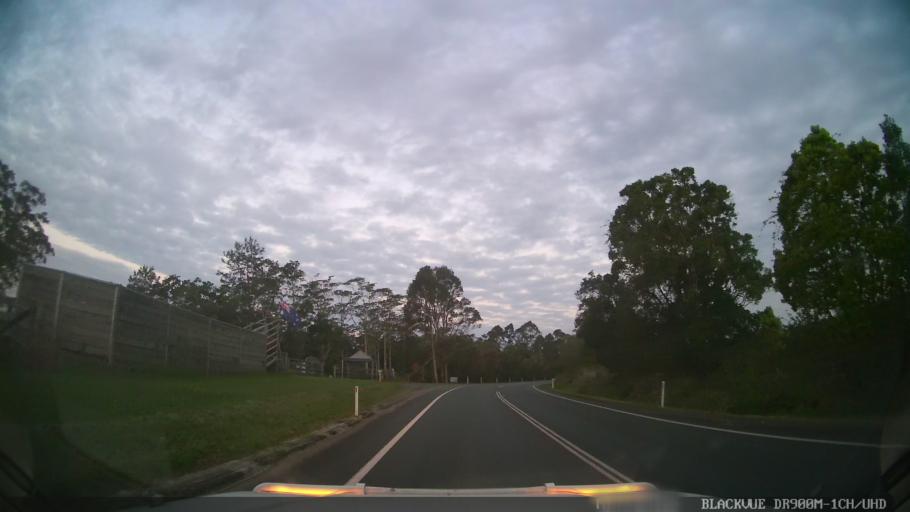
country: AU
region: Queensland
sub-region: Sunshine Coast
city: Nambour
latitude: -26.6184
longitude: 152.9029
